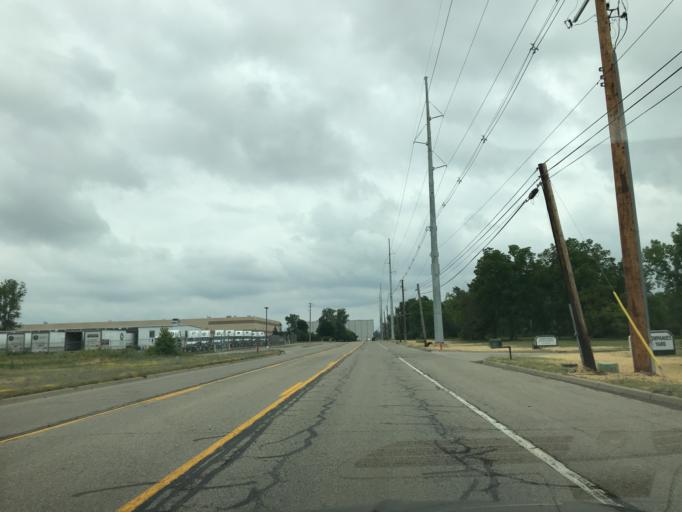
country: US
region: Michigan
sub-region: Eaton County
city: Waverly
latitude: 42.6975
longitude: -84.6502
